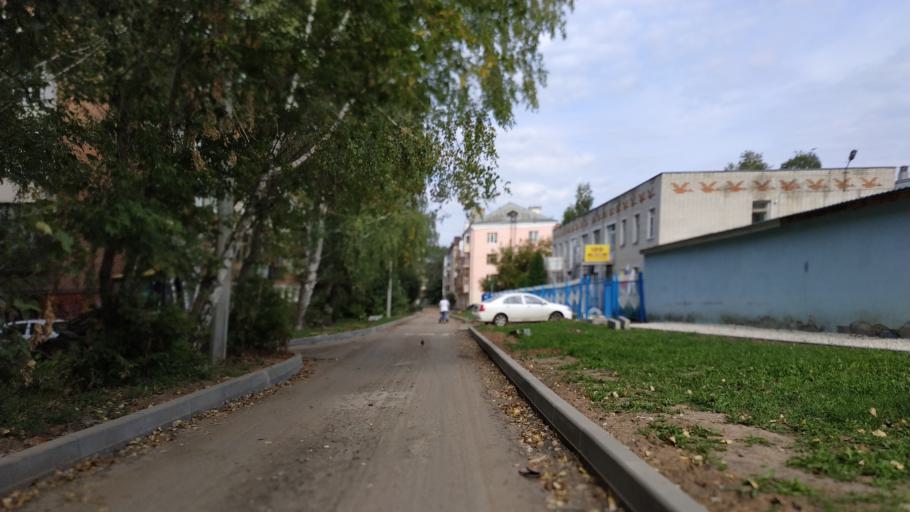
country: RU
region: Chuvashia
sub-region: Cheboksarskiy Rayon
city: Cheboksary
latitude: 56.1481
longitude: 47.2207
